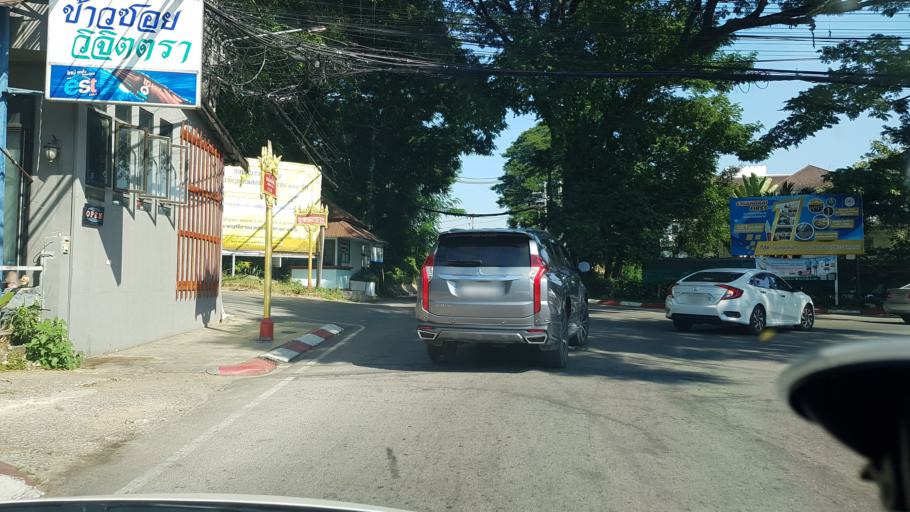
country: TH
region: Chiang Rai
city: Chiang Rai
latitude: 19.9126
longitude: 99.8284
